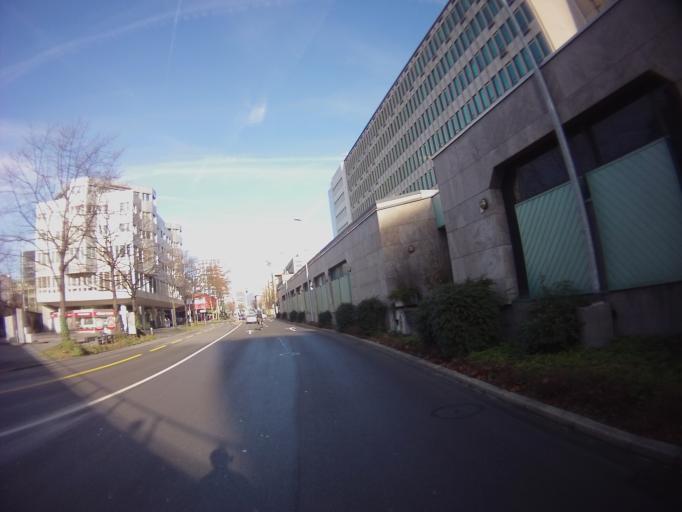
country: CH
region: Zug
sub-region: Zug
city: Zug
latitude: 47.1709
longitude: 8.5160
